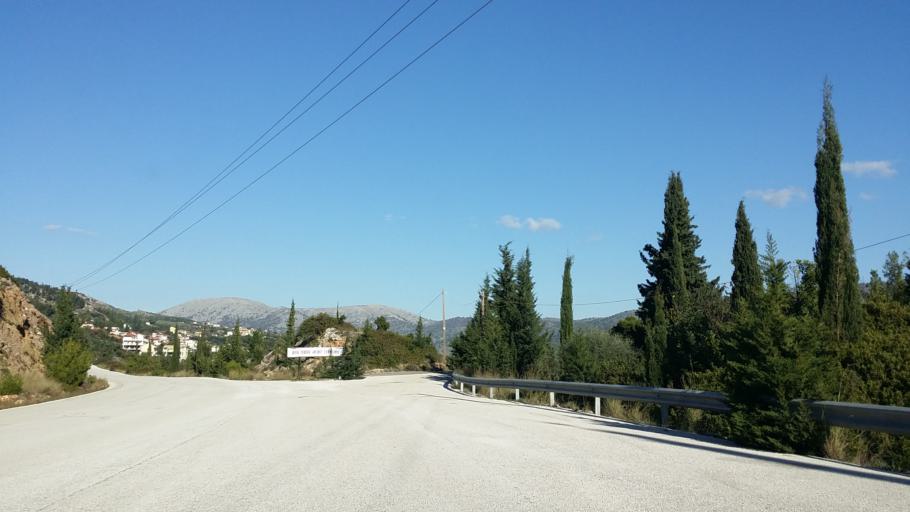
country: GR
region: West Greece
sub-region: Nomos Aitolias kai Akarnanias
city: Astakos
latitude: 38.5245
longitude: 21.0691
